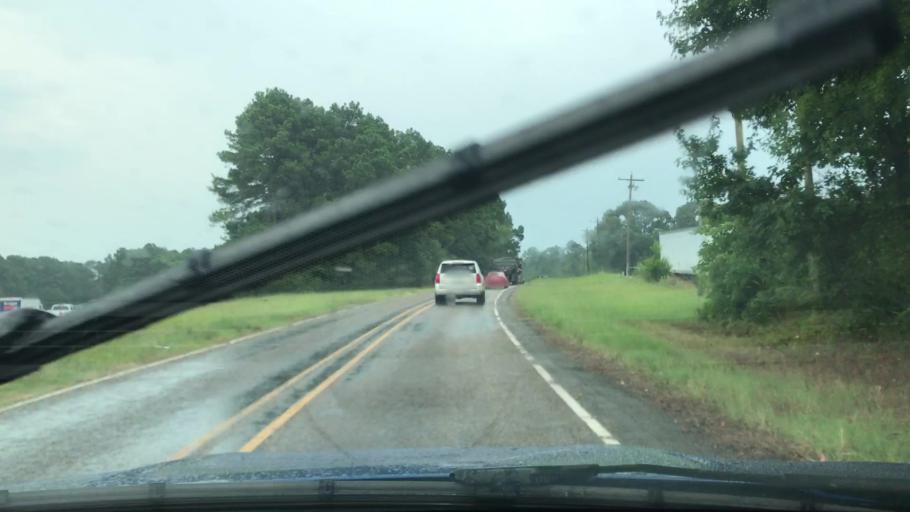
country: US
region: Texas
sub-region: Harrison County
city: Waskom
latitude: 32.4841
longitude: -94.1171
